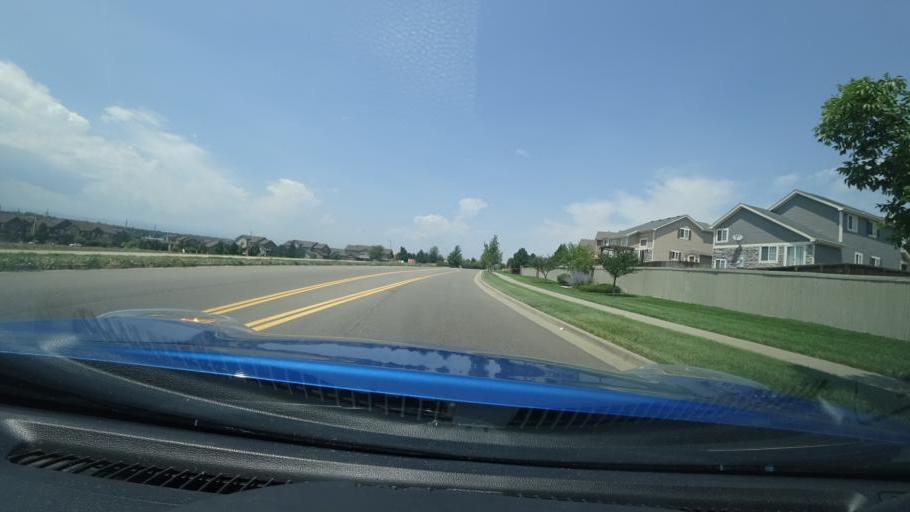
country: US
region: Colorado
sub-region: Adams County
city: Aurora
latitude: 39.6699
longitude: -104.7660
